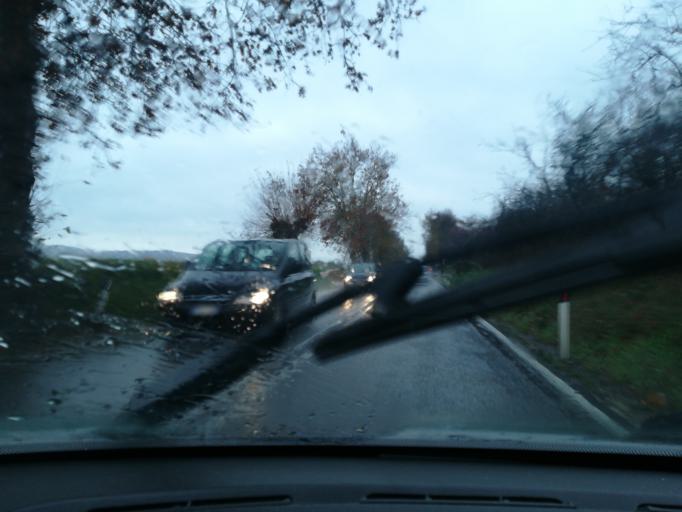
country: IT
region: The Marches
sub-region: Provincia di Macerata
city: Sforzacosta
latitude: 43.2664
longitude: 13.4226
